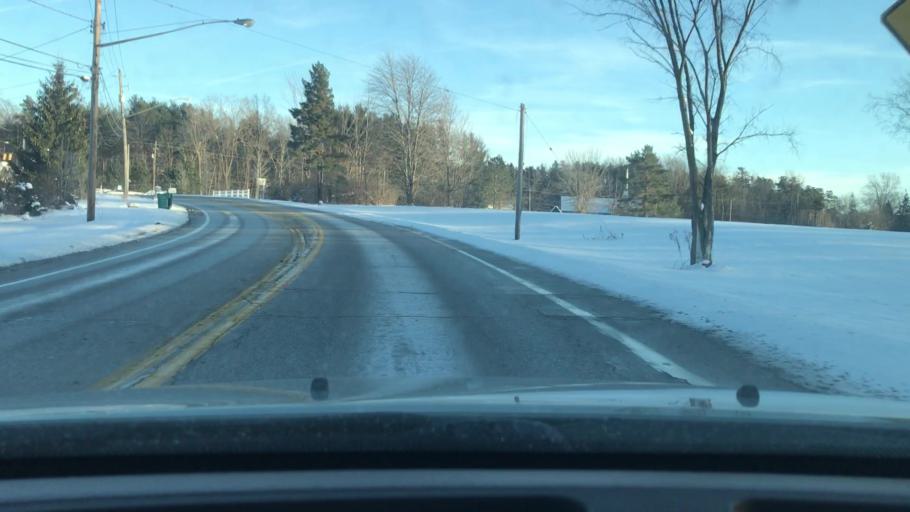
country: US
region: Ohio
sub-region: Lake County
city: Mentor
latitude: 41.6547
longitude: -81.3294
